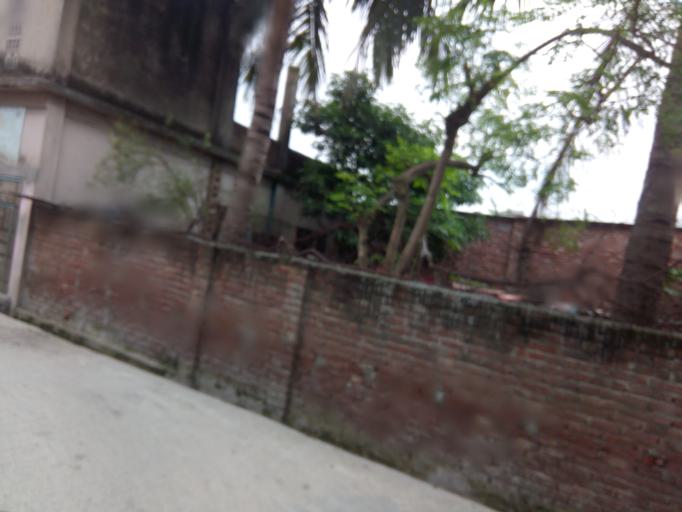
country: BD
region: Dhaka
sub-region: Dhaka
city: Dhaka
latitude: 23.6889
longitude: 90.4456
